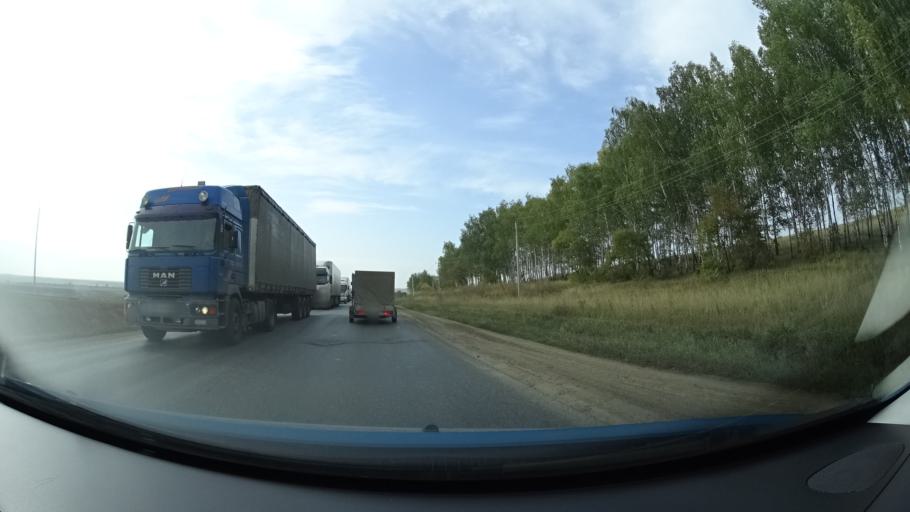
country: RU
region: Bashkortostan
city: Buzdyak
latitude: 54.6348
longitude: 54.4734
